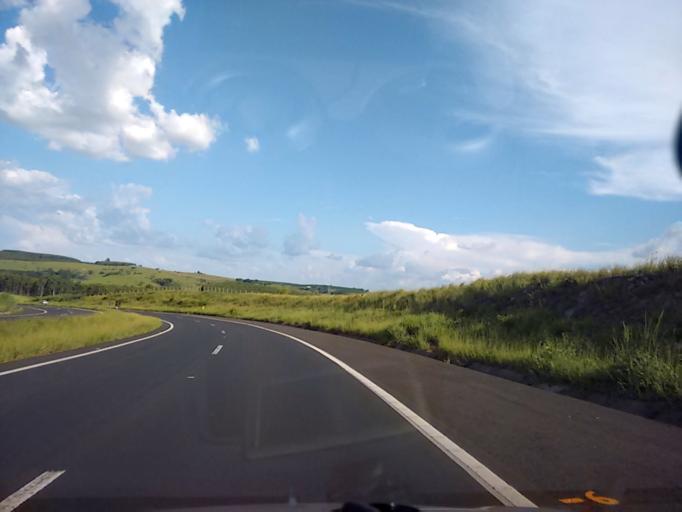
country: BR
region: Sao Paulo
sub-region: Duartina
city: Duartina
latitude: -22.3181
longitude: -49.4921
